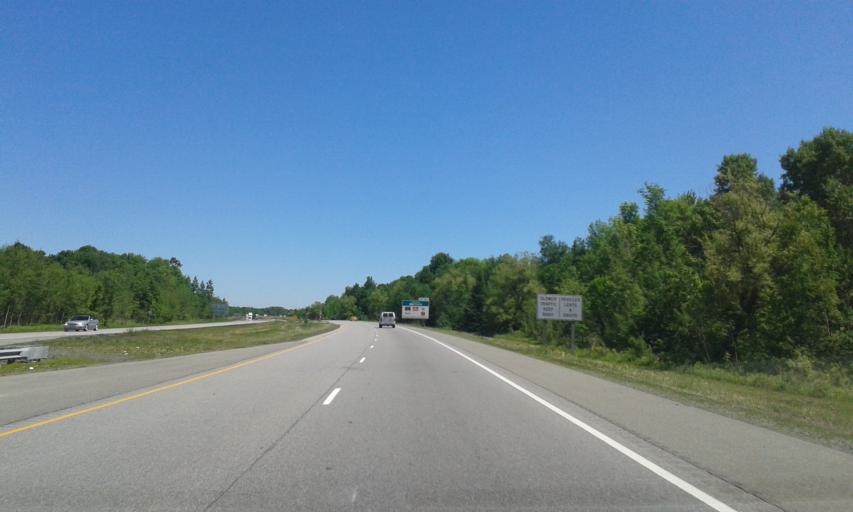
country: CA
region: Ontario
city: Prescott
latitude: 44.7623
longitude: -75.4672
